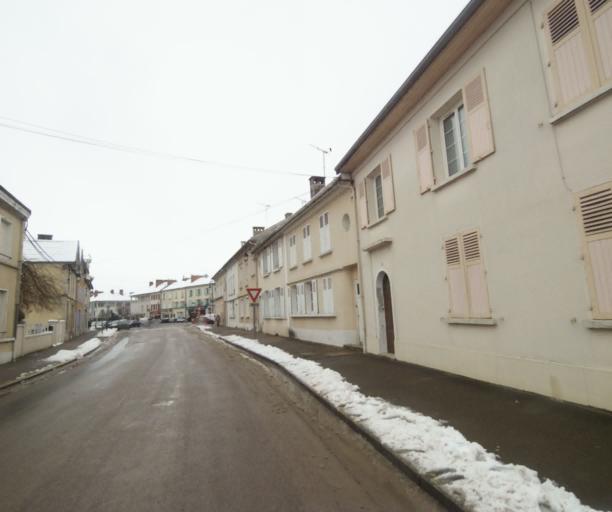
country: FR
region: Champagne-Ardenne
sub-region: Departement de la Haute-Marne
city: Montier-en-Der
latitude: 48.4760
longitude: 4.7722
